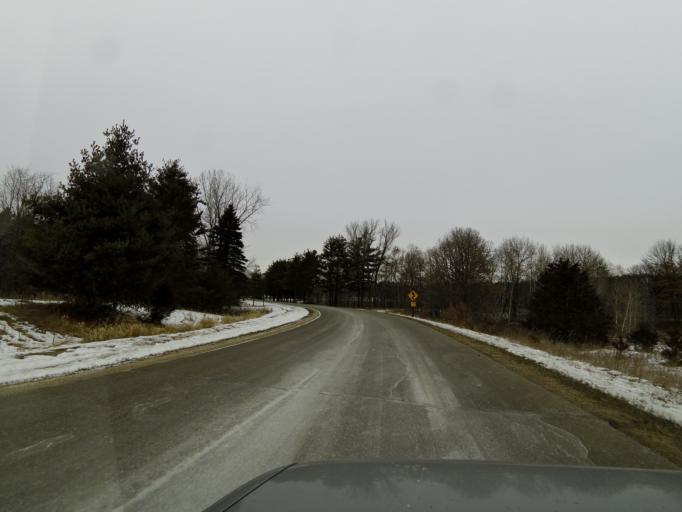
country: US
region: Minnesota
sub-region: Washington County
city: Lake Elmo
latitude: 44.9722
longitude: -92.9034
